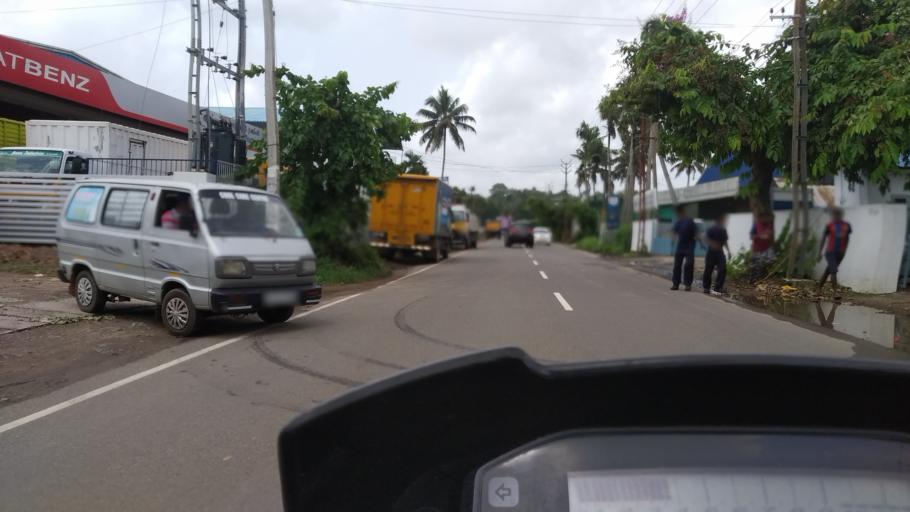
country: IN
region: Kerala
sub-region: Ernakulam
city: Aluva
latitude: 10.1264
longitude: 76.3136
